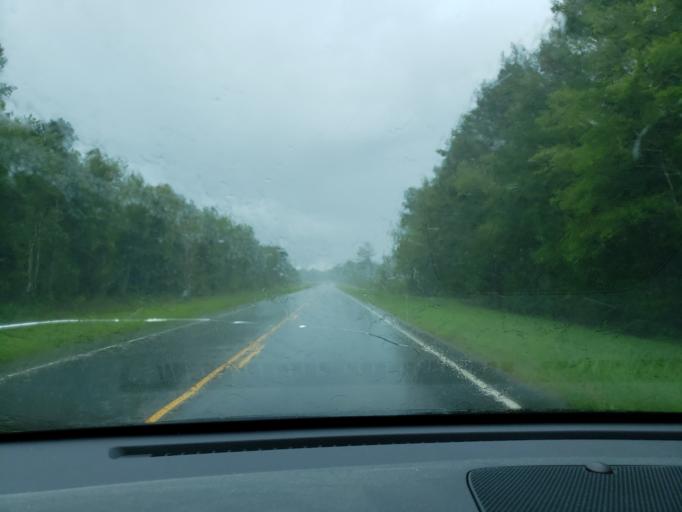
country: US
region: North Carolina
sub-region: Bladen County
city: Elizabethtown
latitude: 34.5303
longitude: -78.6464
